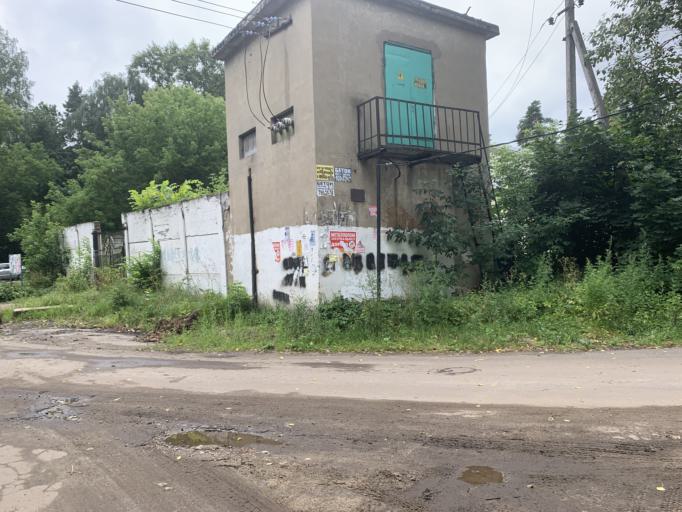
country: RU
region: Moskovskaya
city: Mamontovka
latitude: 55.9758
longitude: 37.8269
